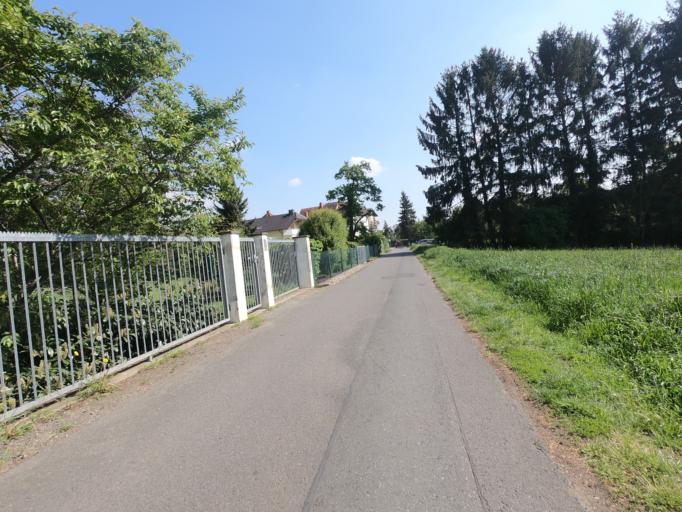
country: DE
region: Hesse
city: Kelsterbach
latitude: 50.0728
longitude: 8.5268
